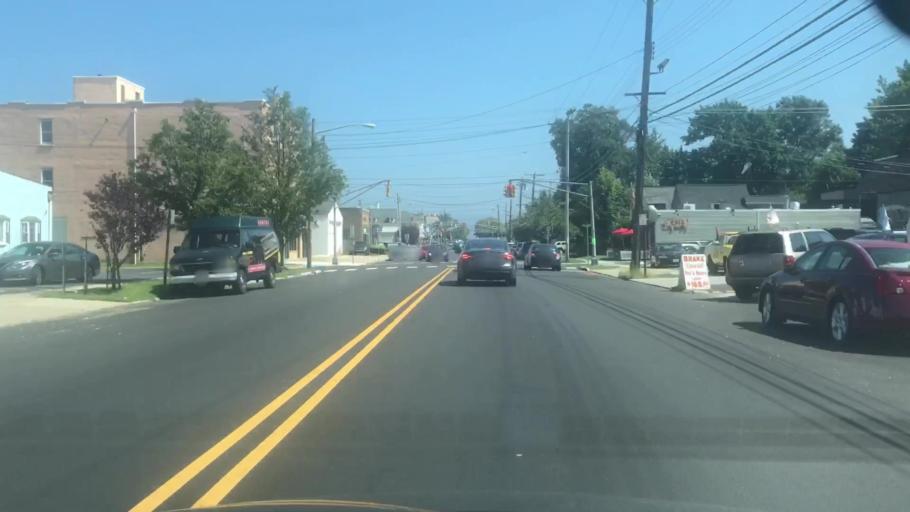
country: US
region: New Jersey
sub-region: Monmouth County
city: Asbury Park
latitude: 40.2211
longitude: -74.0155
